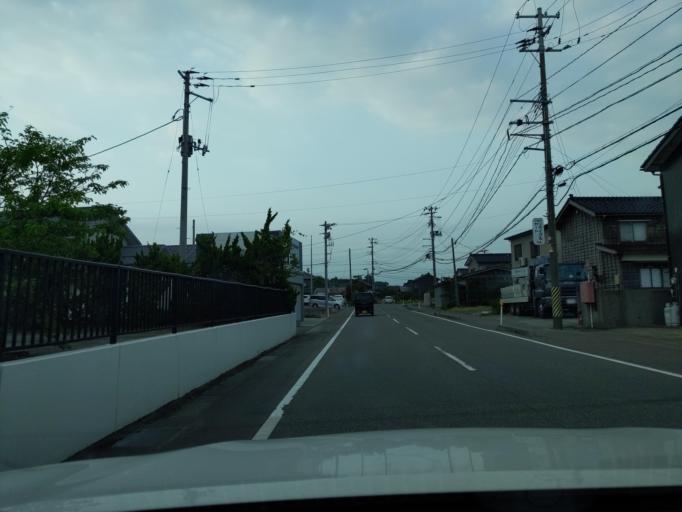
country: JP
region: Niigata
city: Kashiwazaki
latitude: 37.4159
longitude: 138.6121
